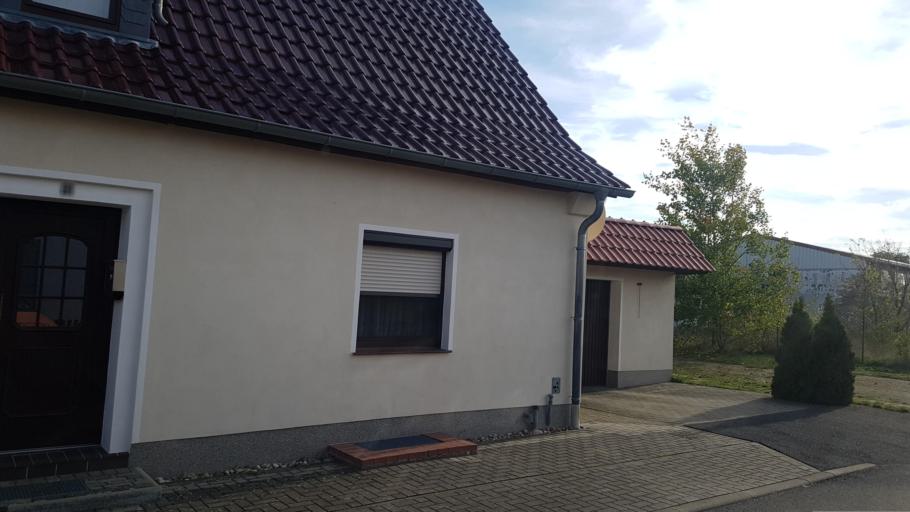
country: DE
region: Brandenburg
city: Schlieben
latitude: 51.7362
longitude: 13.3885
